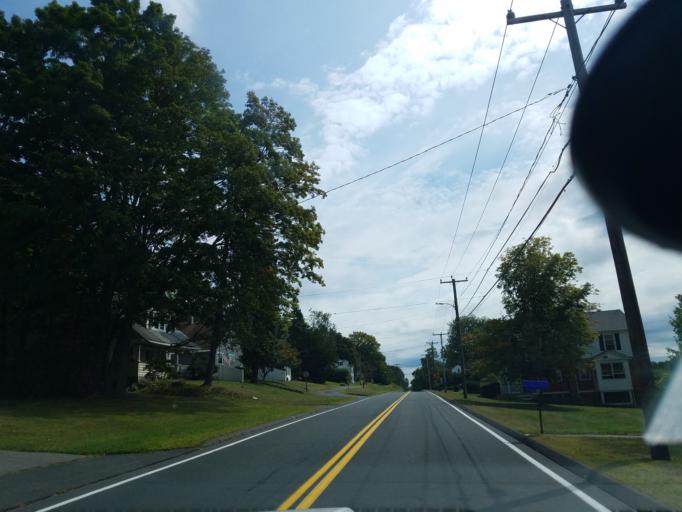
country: US
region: Connecticut
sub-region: Hartford County
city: Wethersfield
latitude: 41.6767
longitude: -72.6444
